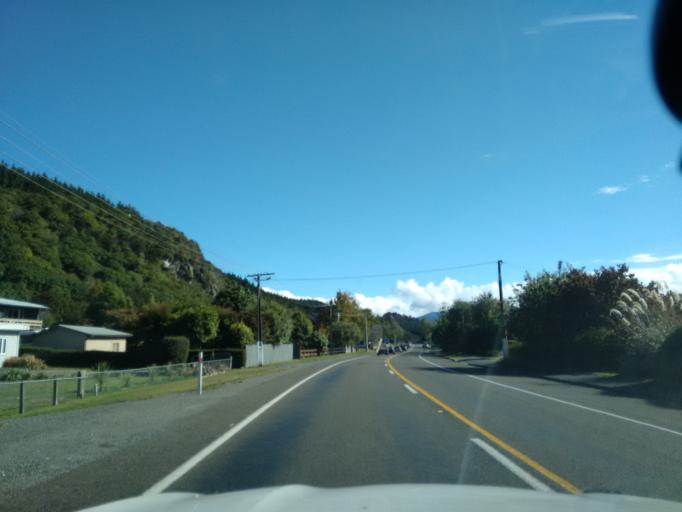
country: NZ
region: Waikato
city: Turangi
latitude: -38.9329
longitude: 175.8749
